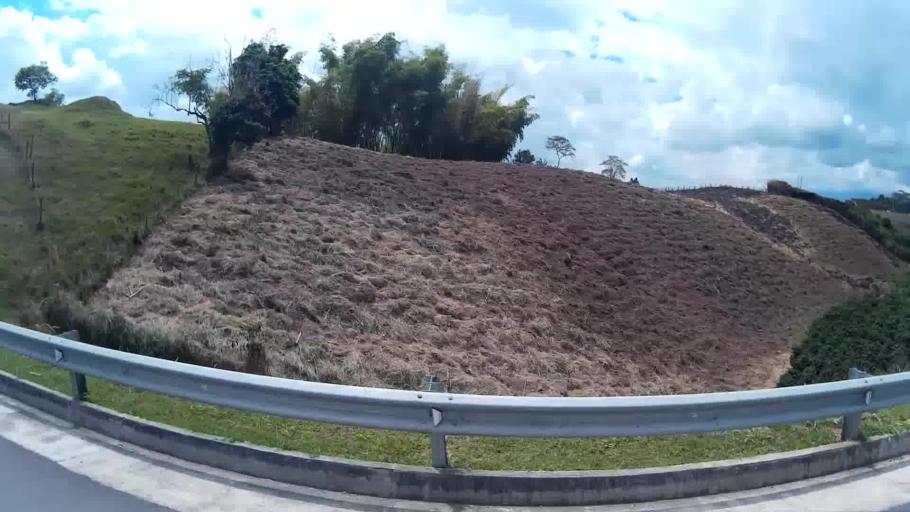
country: CO
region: Risaralda
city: Pereira
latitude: 4.7898
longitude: -75.7442
